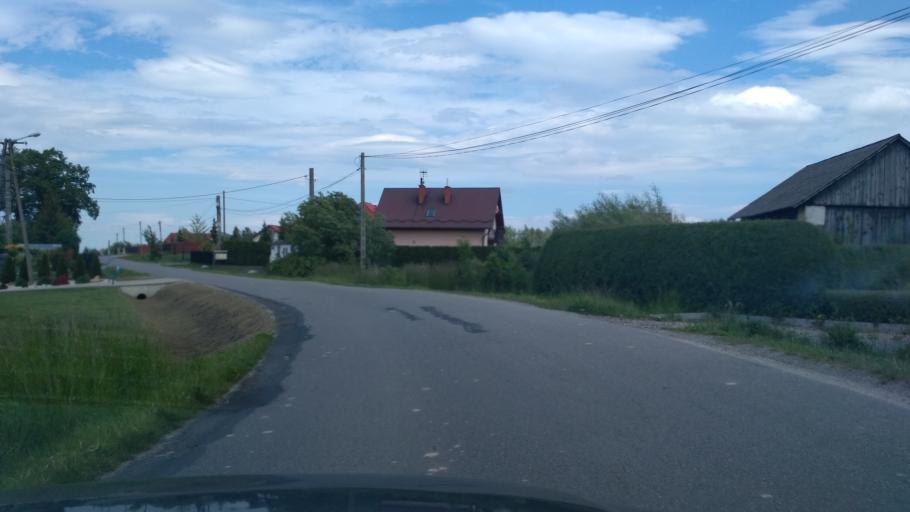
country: PL
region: Subcarpathian Voivodeship
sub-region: Powiat ropczycko-sedziszowski
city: Ropczyce
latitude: 50.0259
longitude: 21.6067
